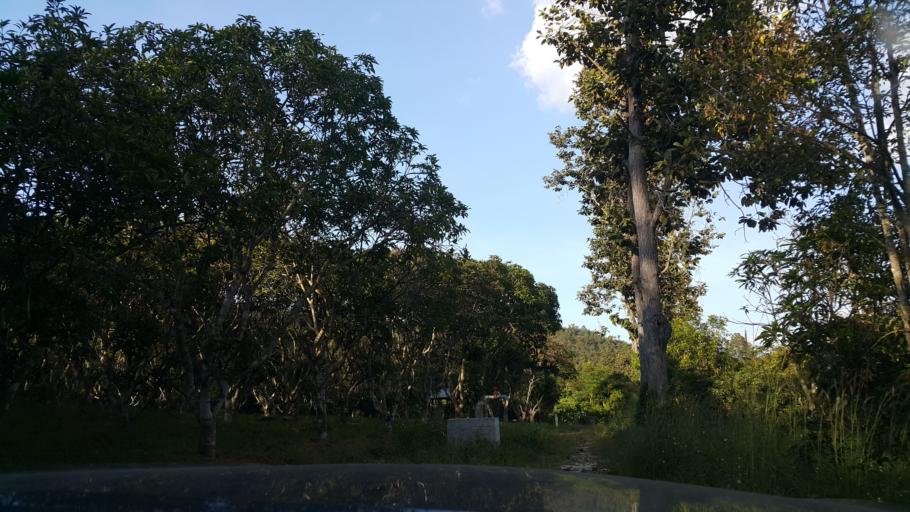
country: TH
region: Chiang Mai
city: San Kamphaeng
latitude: 18.7073
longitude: 99.1952
